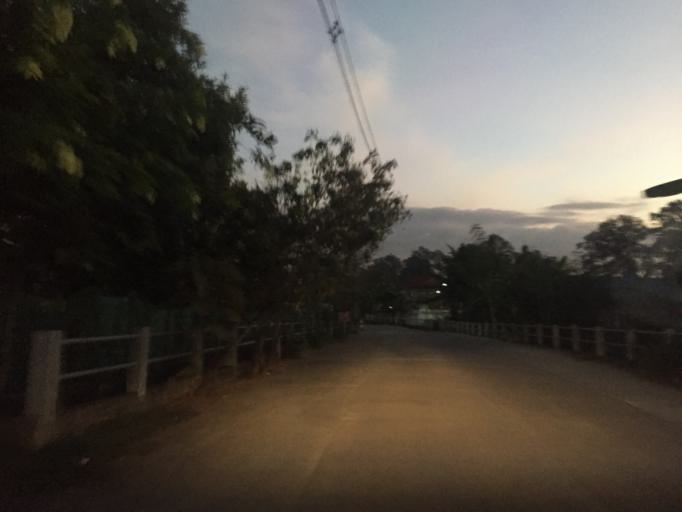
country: TH
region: Chiang Mai
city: Saraphi
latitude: 18.7267
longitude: 99.0268
